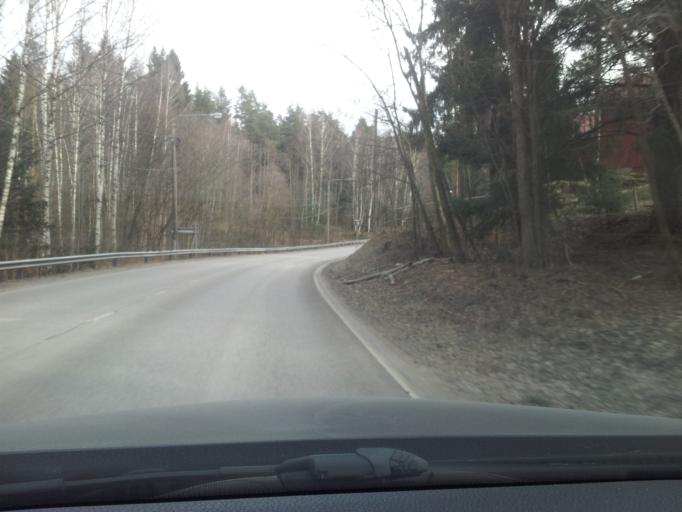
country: FI
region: Uusimaa
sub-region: Helsinki
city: Koukkuniemi
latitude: 60.1849
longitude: 24.7541
